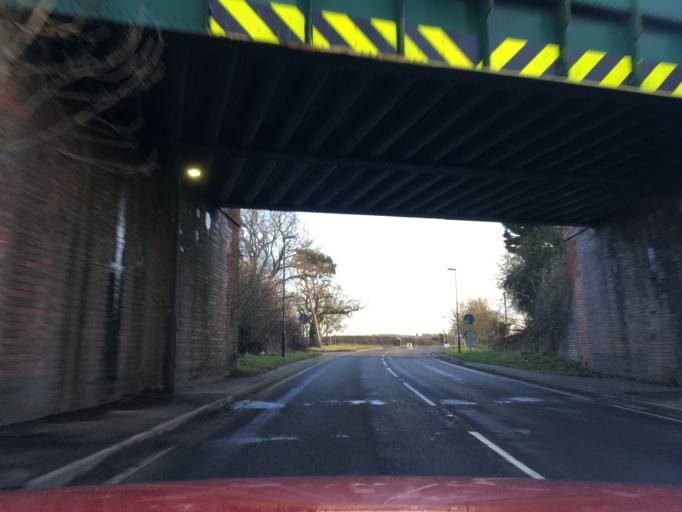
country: GB
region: England
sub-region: Warwickshire
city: Henley in Arden
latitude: 52.2459
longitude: -1.7490
